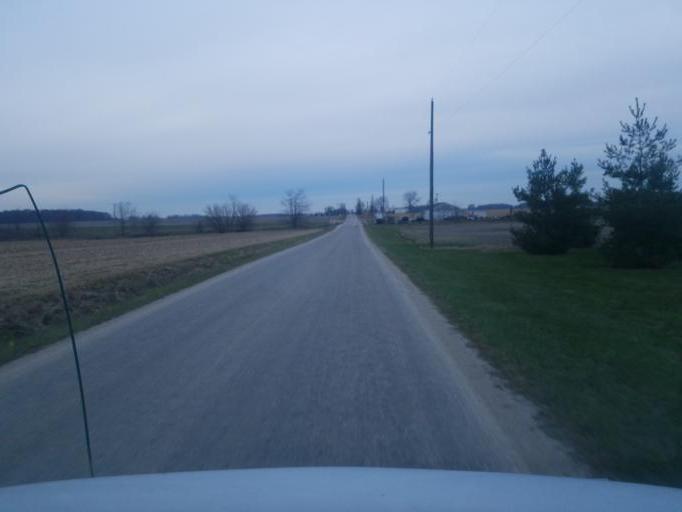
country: US
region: Indiana
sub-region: Adams County
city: Decatur
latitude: 40.7440
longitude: -84.8796
